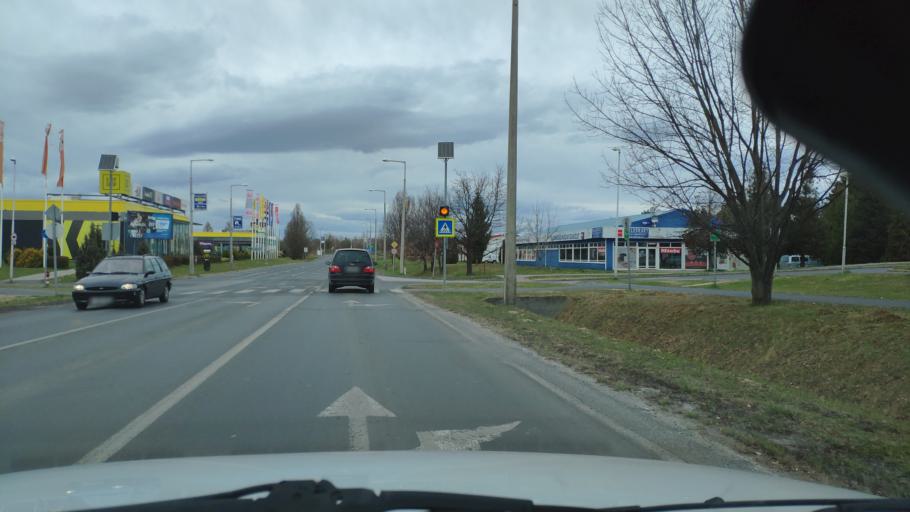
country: HU
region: Zala
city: Nagykanizsa
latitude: 46.4626
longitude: 17.0088
